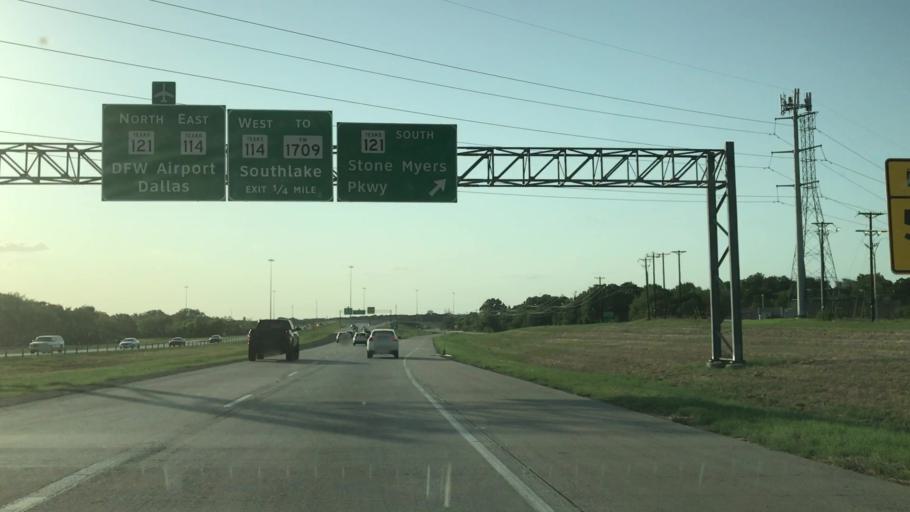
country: US
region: Texas
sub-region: Tarrant County
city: Grapevine
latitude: 32.8987
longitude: -97.0906
